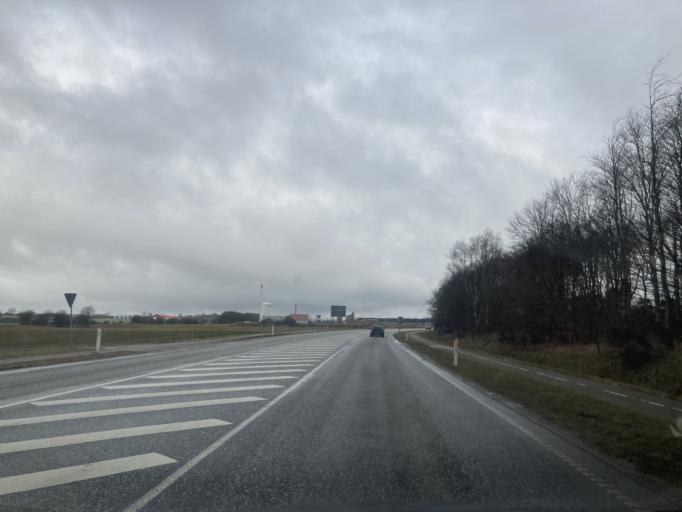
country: DK
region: Zealand
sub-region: Slagelse Kommune
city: Slagelse
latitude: 55.3783
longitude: 11.3760
